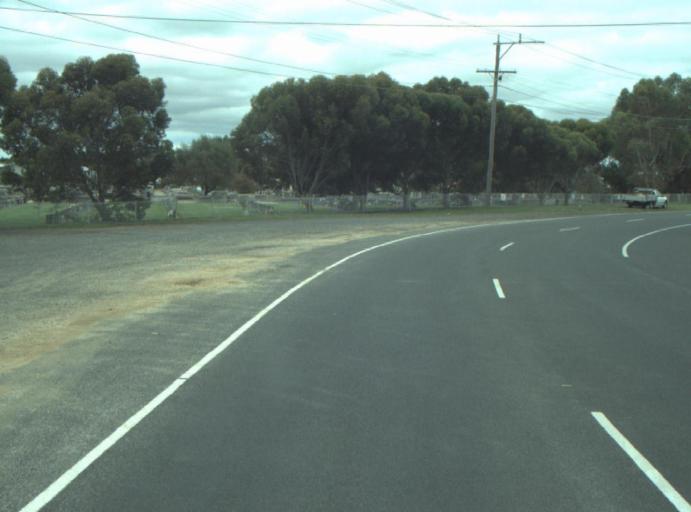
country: AU
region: Victoria
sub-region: Greater Geelong
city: East Geelong
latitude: -38.1609
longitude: 144.3799
